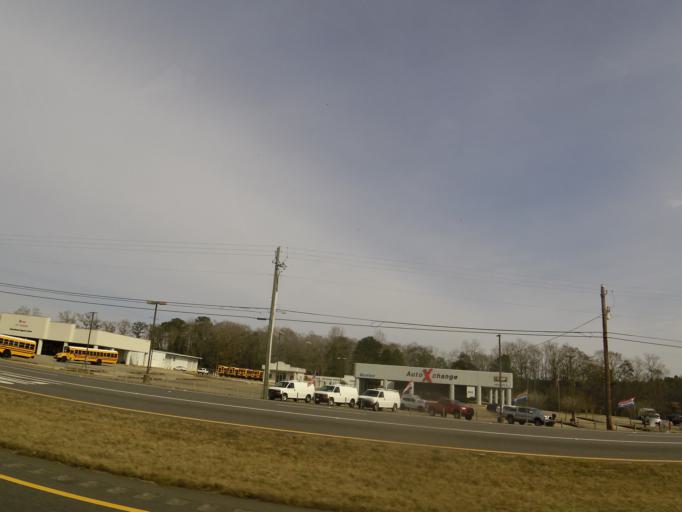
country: US
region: Alabama
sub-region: Dale County
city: Ozark
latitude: 31.4671
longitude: -85.6753
